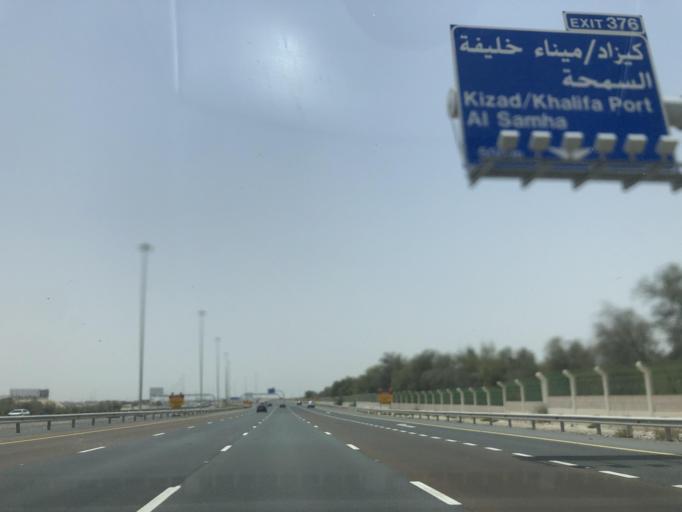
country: AE
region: Abu Dhabi
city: Abu Dhabi
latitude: 24.7057
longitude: 54.7876
